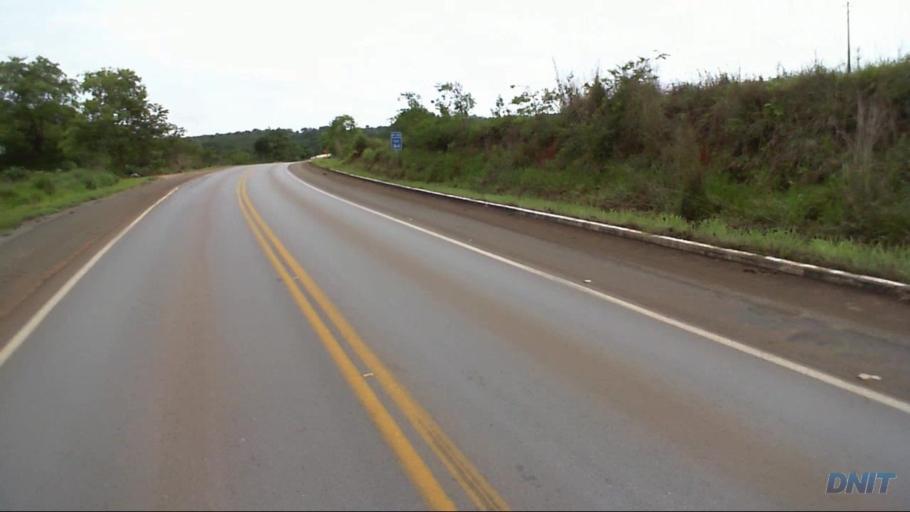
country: BR
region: Goias
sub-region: Uruacu
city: Uruacu
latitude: -14.7513
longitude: -49.0729
